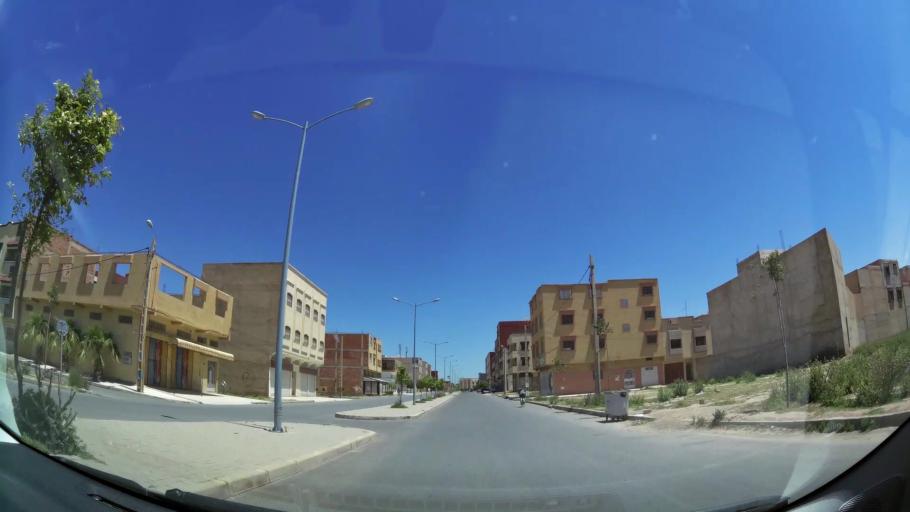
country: MA
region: Oriental
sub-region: Oujda-Angad
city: Oujda
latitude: 34.6753
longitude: -1.8638
